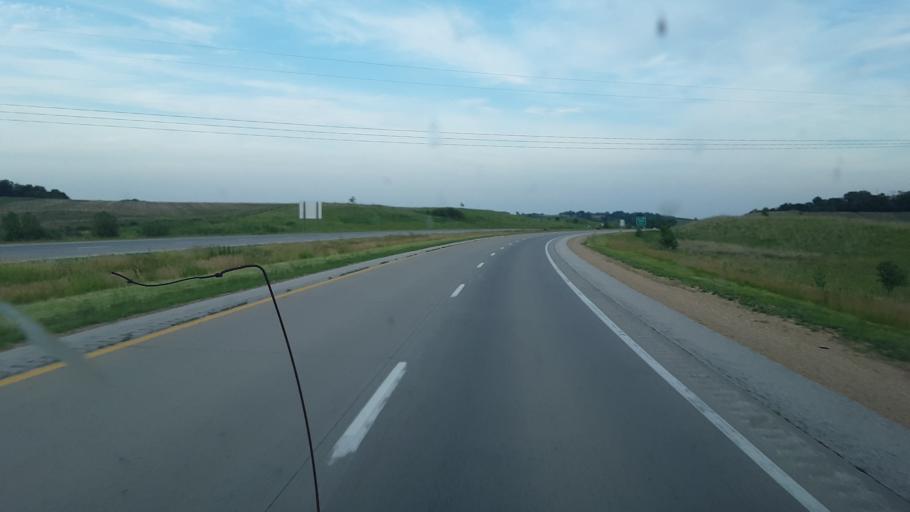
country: US
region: Iowa
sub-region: Tama County
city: Toledo
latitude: 41.9815
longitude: -92.5675
